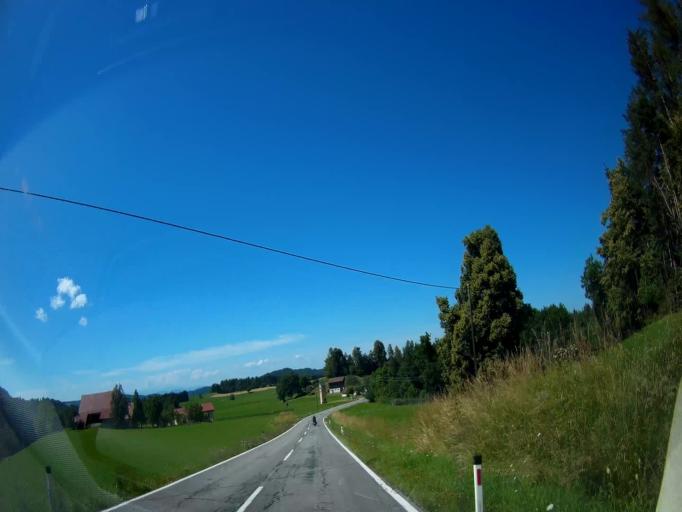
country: AT
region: Carinthia
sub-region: Politischer Bezirk Volkermarkt
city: Gallizien
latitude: 46.5456
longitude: 14.4711
